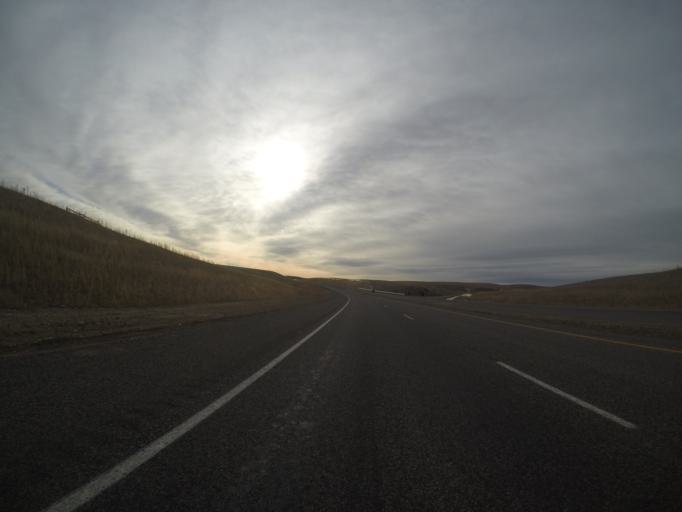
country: US
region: Montana
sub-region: Yellowstone County
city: Laurel
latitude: 45.5508
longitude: -108.8630
